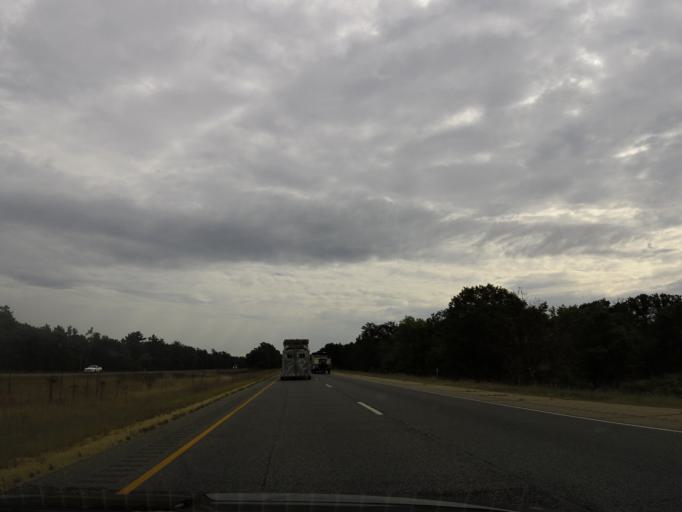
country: US
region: Wisconsin
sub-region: Monroe County
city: Sparta
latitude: 43.9422
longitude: -90.6757
